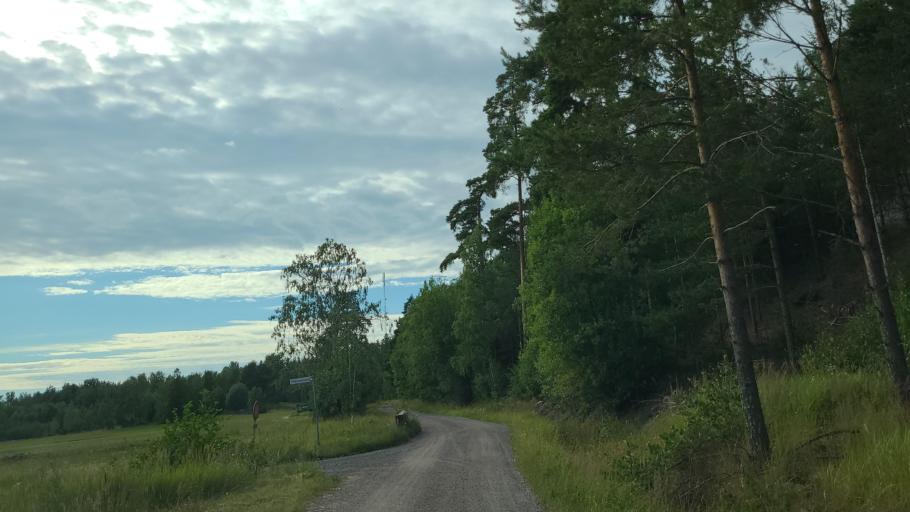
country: FI
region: Varsinais-Suomi
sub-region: Aboland-Turunmaa
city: Nagu
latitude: 60.2822
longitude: 21.9385
